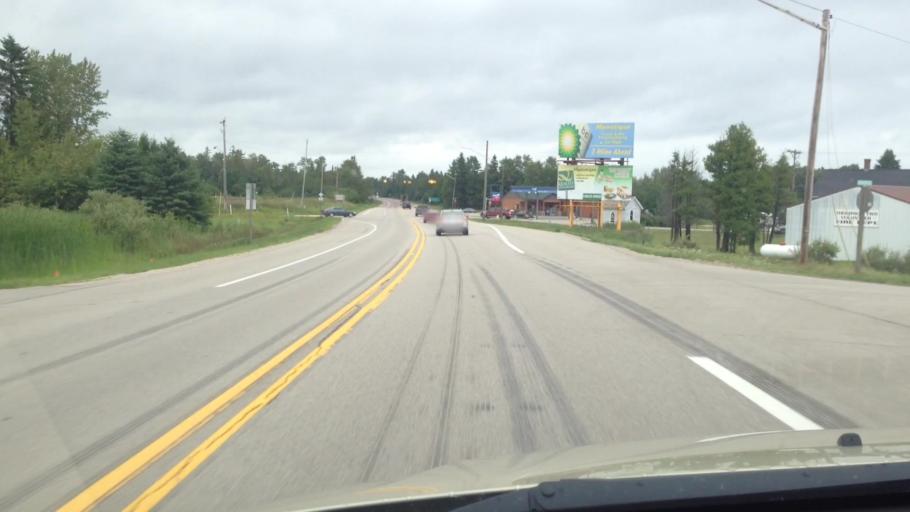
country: US
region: Michigan
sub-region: Schoolcraft County
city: Manistique
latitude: 45.9052
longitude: -86.3304
